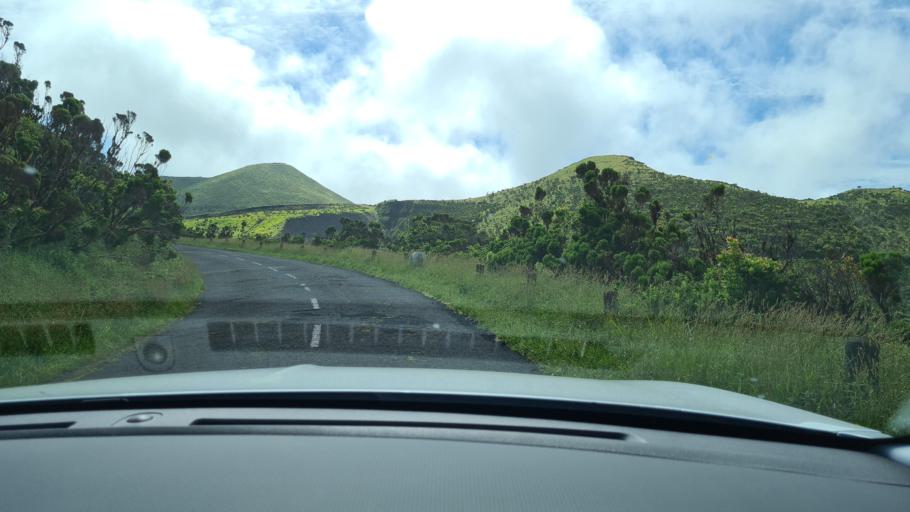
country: PT
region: Azores
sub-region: Sao Roque do Pico
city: Sao Roque do Pico
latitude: 38.6684
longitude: -28.1220
